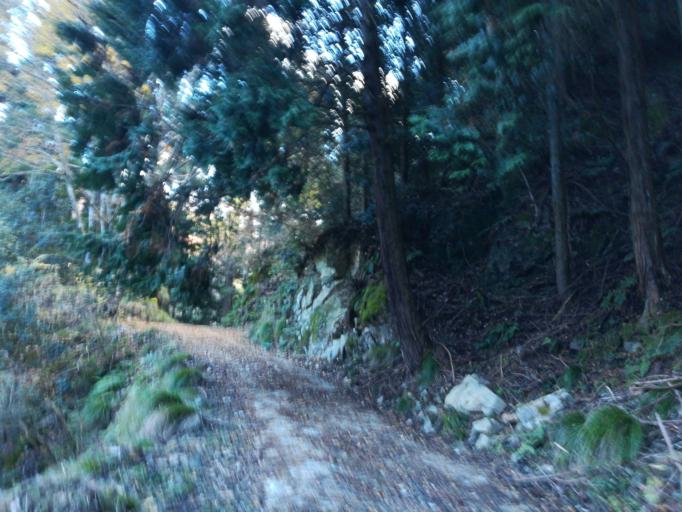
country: JP
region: Kyoto
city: Kameoka
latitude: 34.9833
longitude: 135.6272
